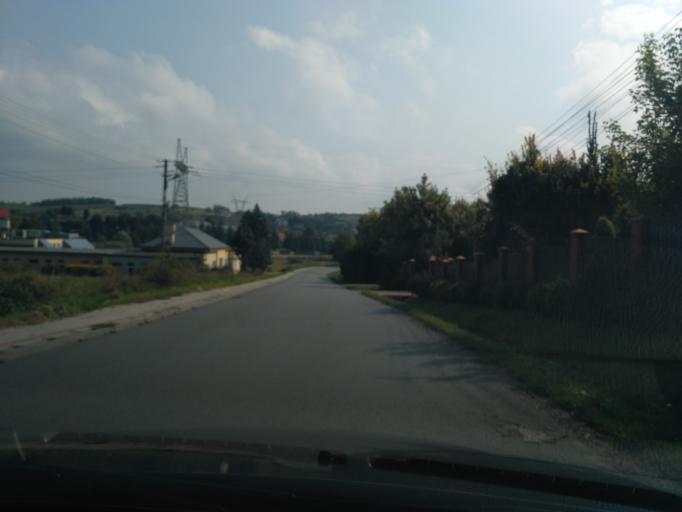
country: PL
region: Subcarpathian Voivodeship
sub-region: Powiat rzeszowski
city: Niechobrz
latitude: 50.0067
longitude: 21.9004
